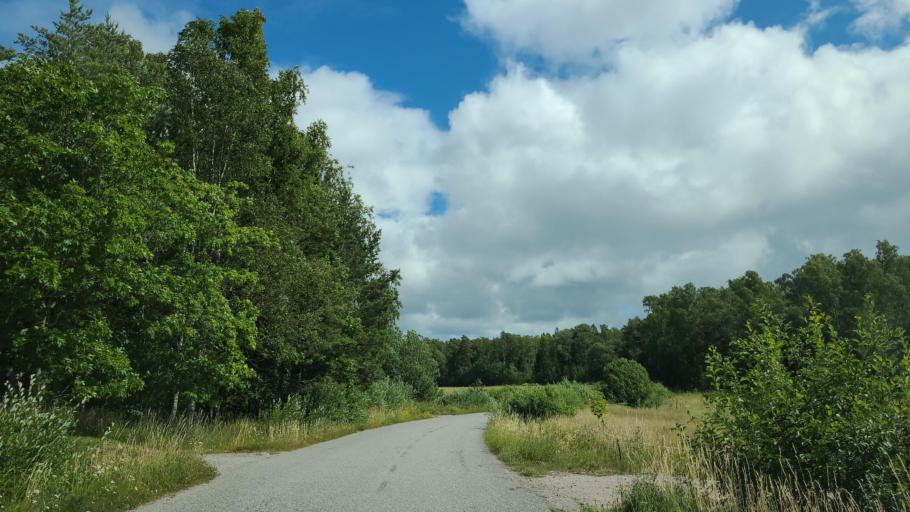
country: FI
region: Varsinais-Suomi
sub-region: Aboland-Turunmaa
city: Nagu
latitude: 60.1759
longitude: 22.0247
